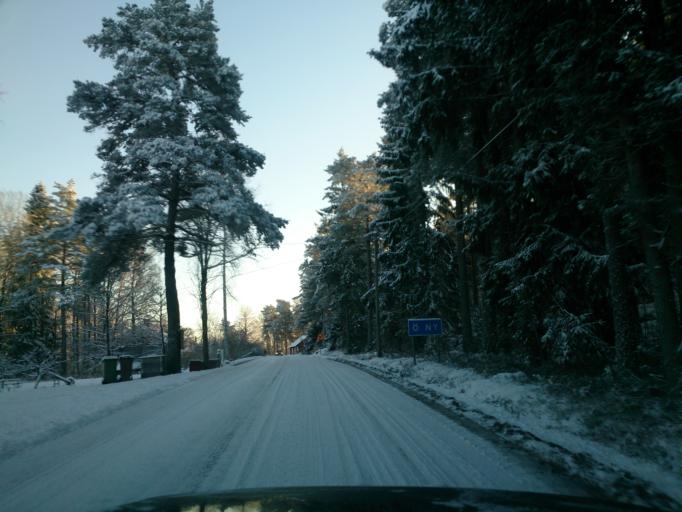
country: SE
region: OEstergoetland
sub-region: Norrkopings Kommun
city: Krokek
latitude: 58.4954
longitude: 16.5507
